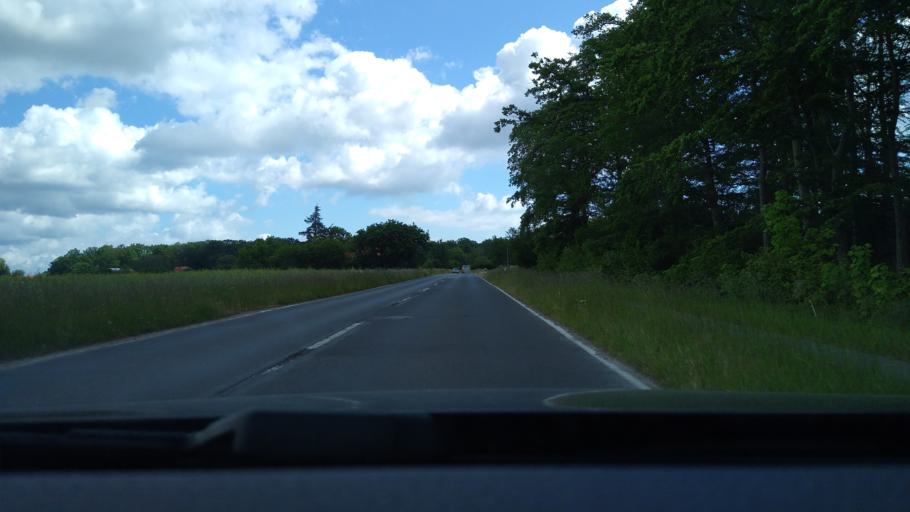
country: DE
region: Schleswig-Holstein
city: Kellenhusen
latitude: 54.2115
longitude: 11.0493
